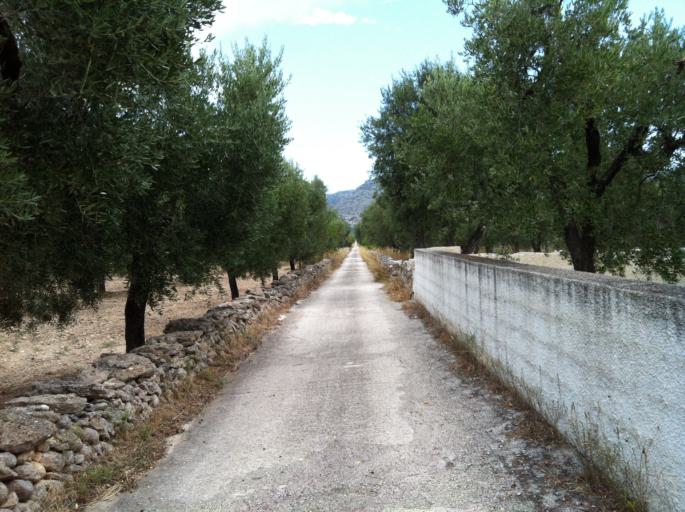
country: IT
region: Apulia
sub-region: Provincia di Foggia
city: Manfredonia
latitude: 41.6528
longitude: 15.9565
